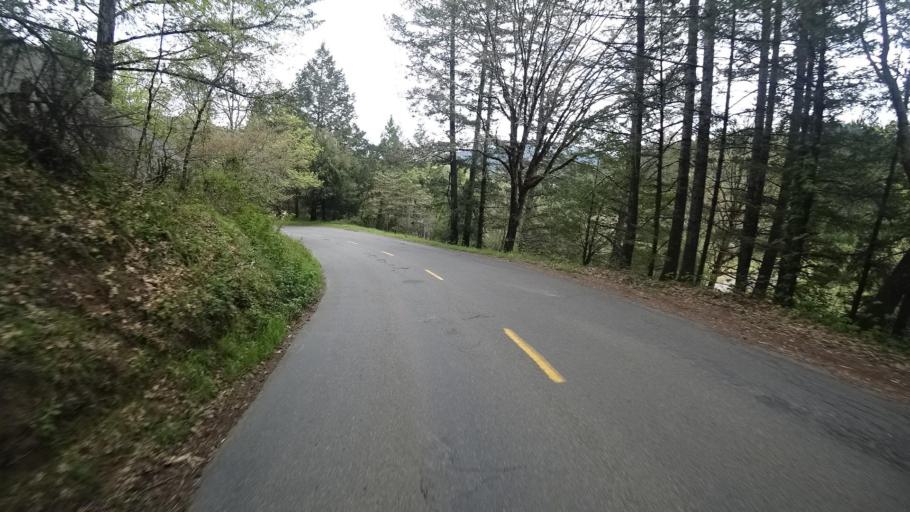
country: US
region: California
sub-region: Humboldt County
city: Redway
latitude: 40.1019
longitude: -123.9075
